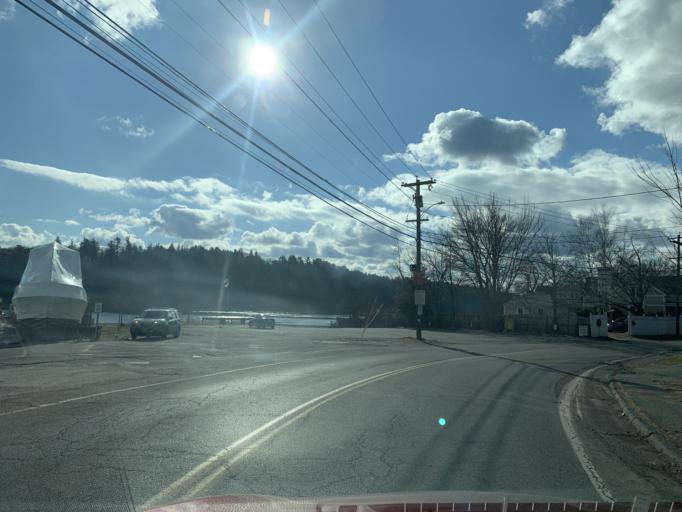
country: US
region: Massachusetts
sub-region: Essex County
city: Amesbury
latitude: 42.8408
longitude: -70.9258
